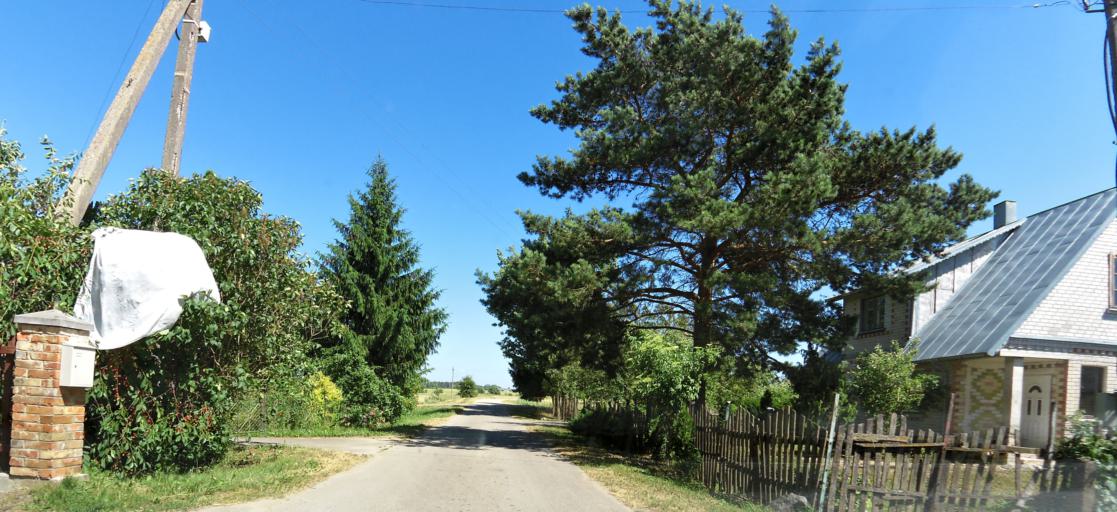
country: LT
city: Vabalninkas
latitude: 55.9820
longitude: 24.7551
